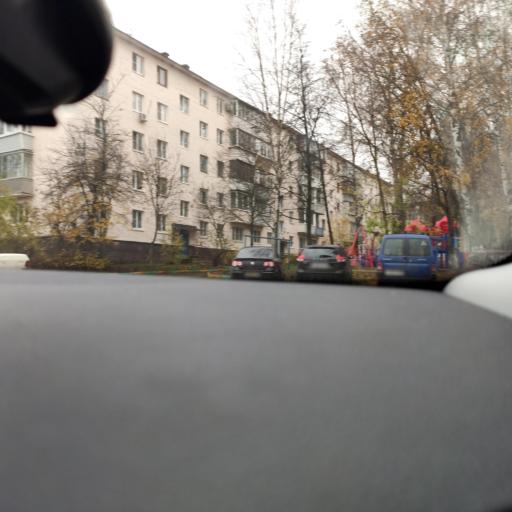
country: RU
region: Moskovskaya
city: Dedovsk
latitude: 55.8557
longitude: 37.1229
